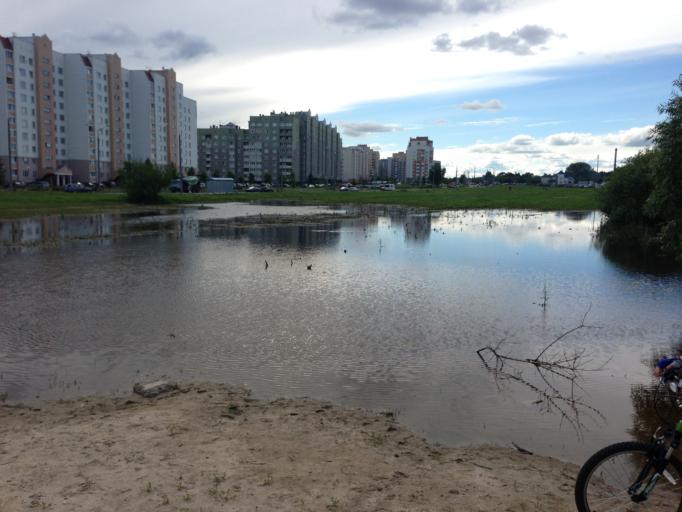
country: BY
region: Grodnenskaya
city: Hrodna
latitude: 53.7157
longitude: 23.8592
